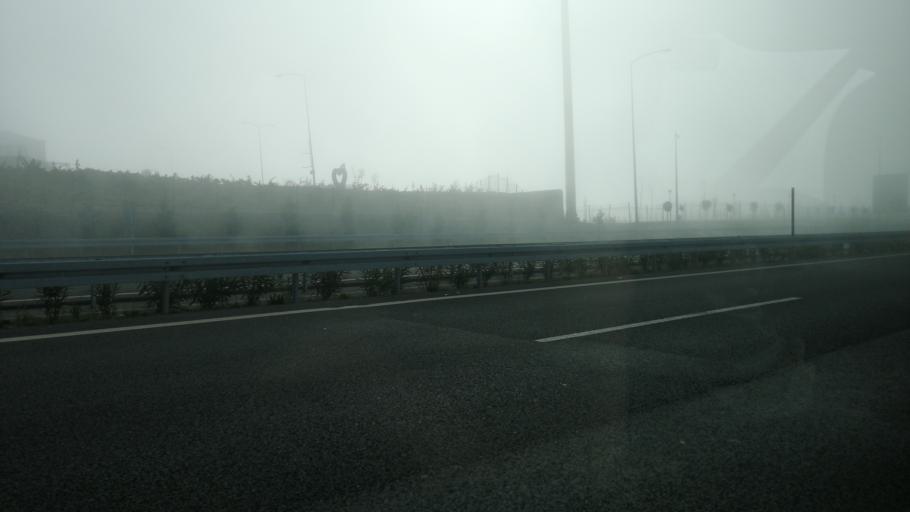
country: TR
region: Kocaeli
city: Tavsanli
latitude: 40.7720
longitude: 29.5183
